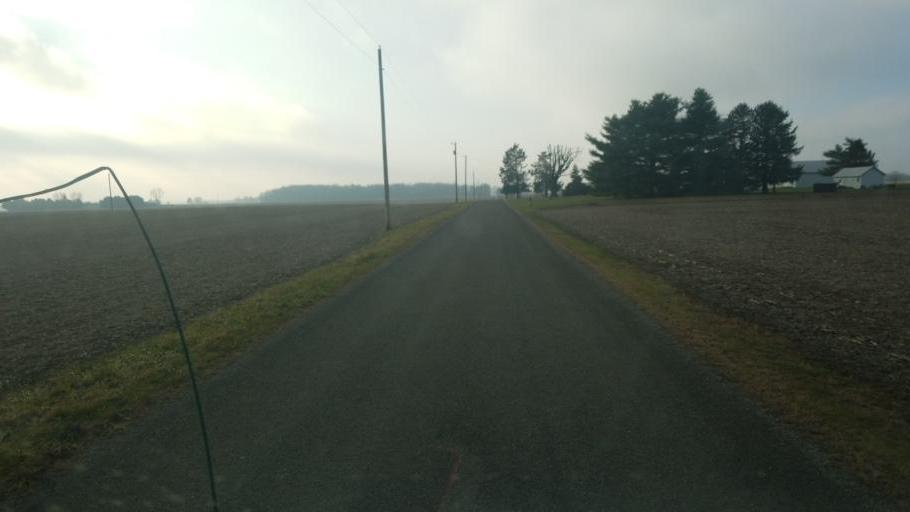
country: US
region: Ohio
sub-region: Hardin County
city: Kenton
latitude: 40.6884
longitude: -83.5878
